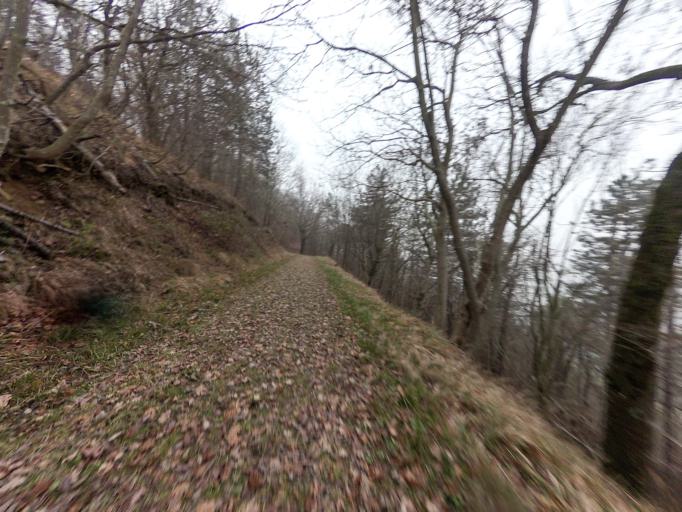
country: IT
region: Emilia-Romagna
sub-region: Provincia di Bologna
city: Pianoro
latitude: 44.3407
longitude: 11.3215
